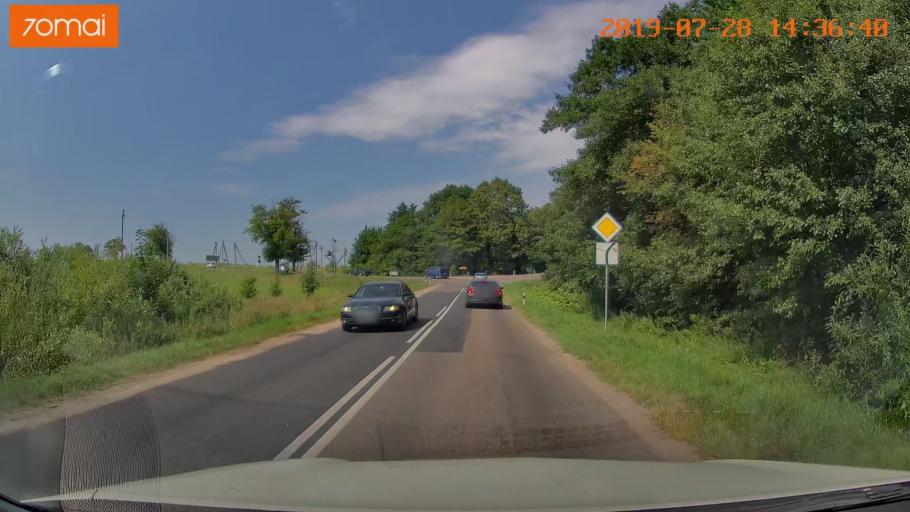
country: RU
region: Kaliningrad
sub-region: Gorod Kaliningrad
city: Yantarnyy
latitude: 54.8391
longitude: 20.0063
